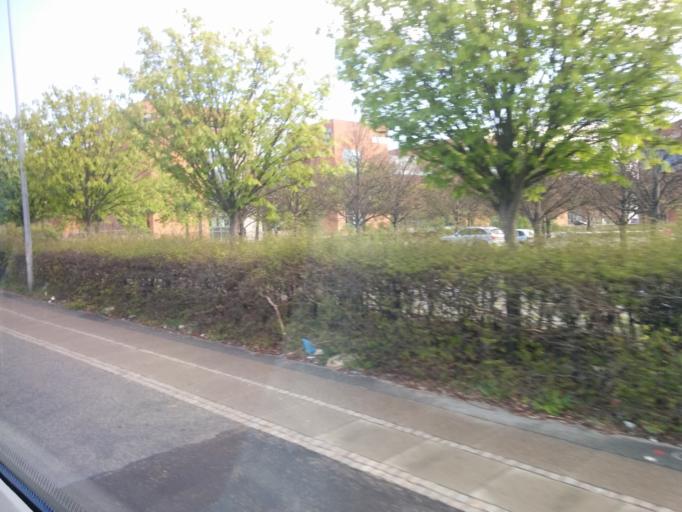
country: DK
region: Central Jutland
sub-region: Arhus Kommune
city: Arhus
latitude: 56.1708
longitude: 10.2054
